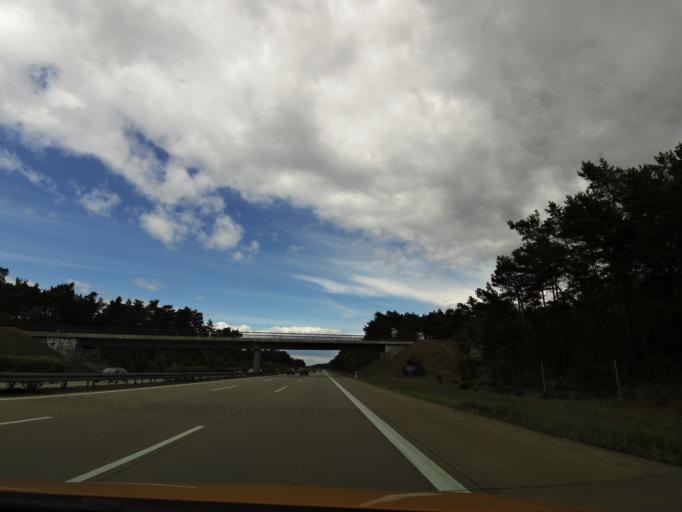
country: DE
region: Brandenburg
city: Wollin
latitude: 52.3052
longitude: 12.4770
